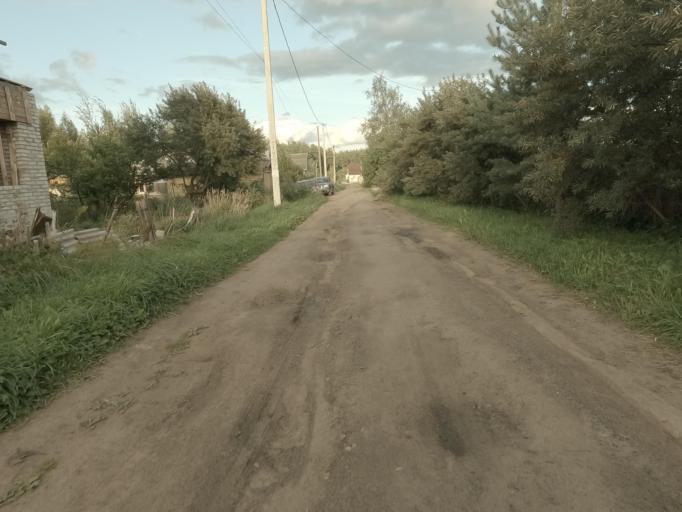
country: RU
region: Leningrad
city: Mga
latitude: 59.7623
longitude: 31.0722
